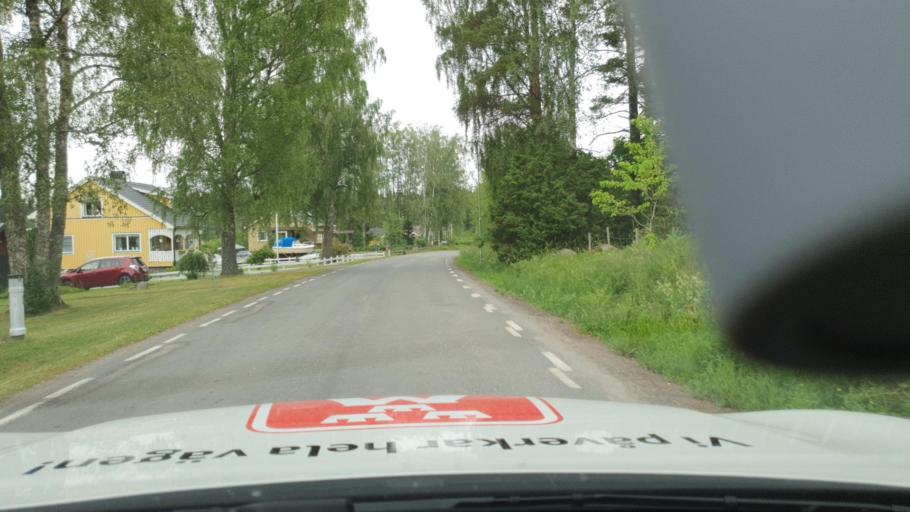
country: SE
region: Vaestra Goetaland
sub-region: Tibro Kommun
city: Tibro
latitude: 58.3721
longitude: 14.0490
